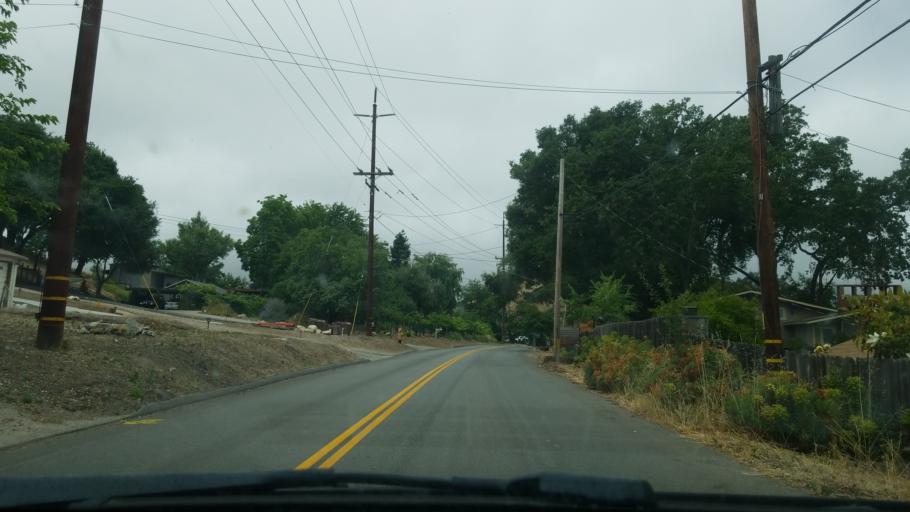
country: US
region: California
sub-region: San Luis Obispo County
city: Atascadero
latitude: 35.4630
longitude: -120.6678
